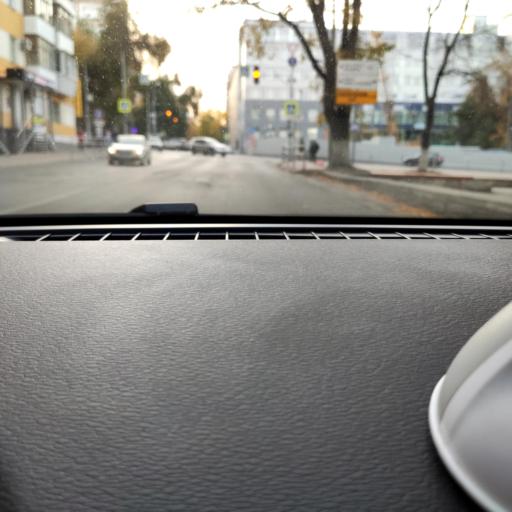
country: RU
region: Samara
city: Samara
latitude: 53.2070
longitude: 50.1265
